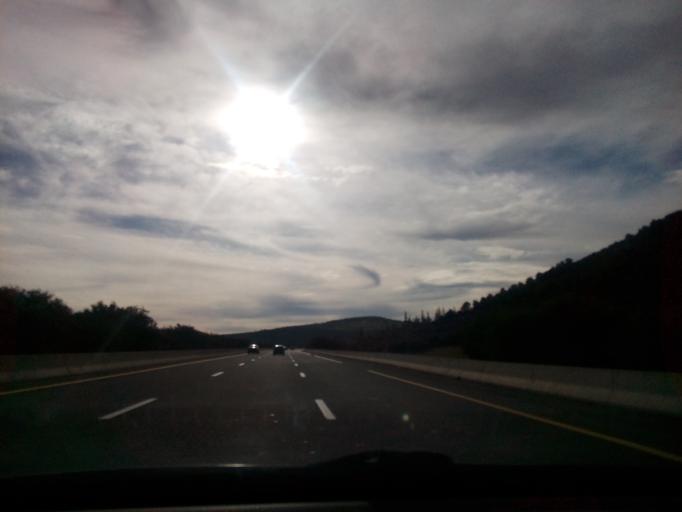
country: DZ
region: Sidi Bel Abbes
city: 'Ain el Berd
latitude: 35.3975
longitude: -0.4900
